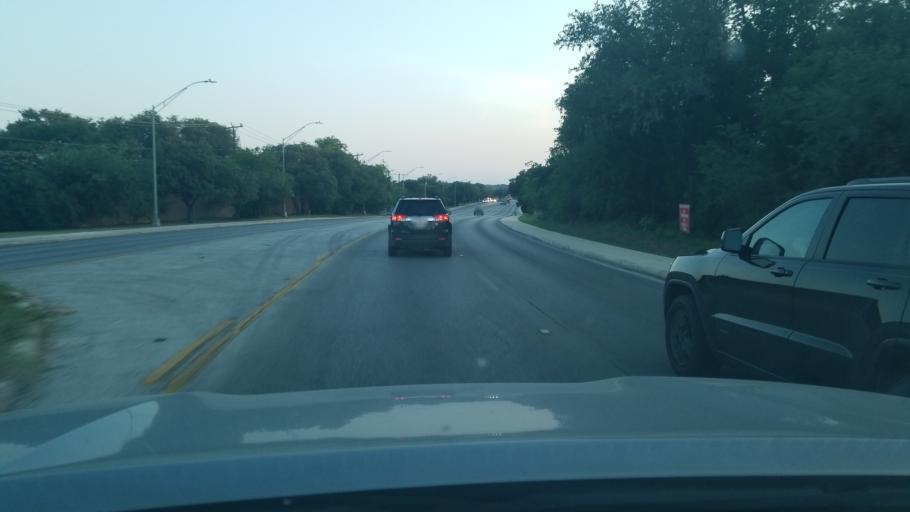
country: US
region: Texas
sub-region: Bexar County
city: Shavano Park
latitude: 29.5790
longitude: -98.5407
